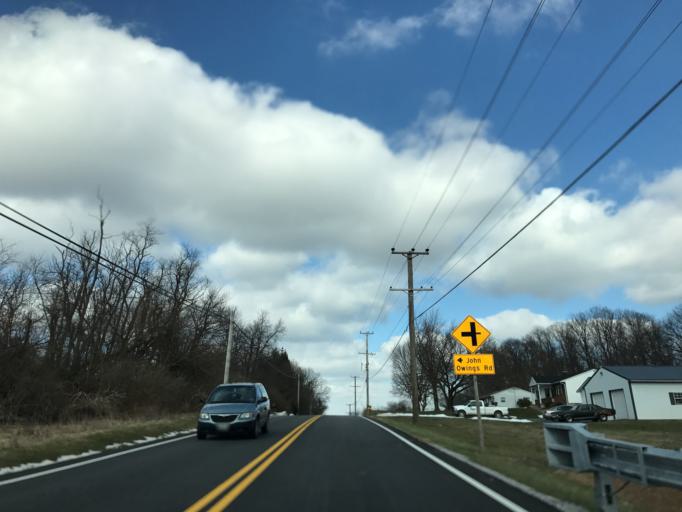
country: US
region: Maryland
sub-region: Carroll County
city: Westminster
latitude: 39.6442
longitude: -76.9773
